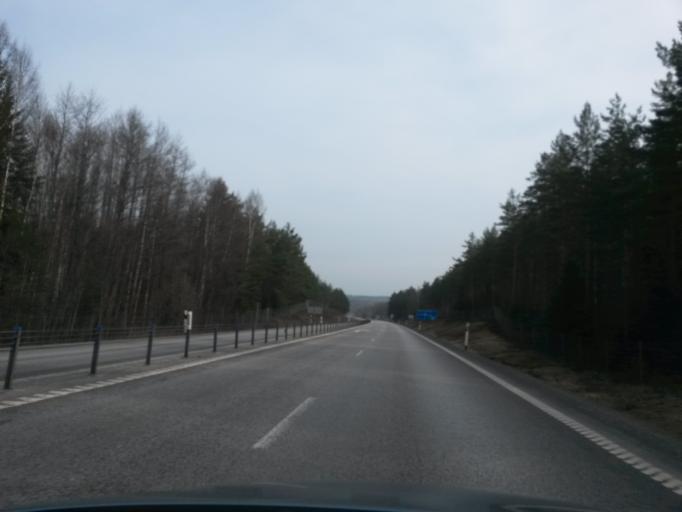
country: SE
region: Vaestra Goetaland
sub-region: Gullspangs Kommun
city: Anderstorp
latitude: 58.9242
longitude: 14.4100
